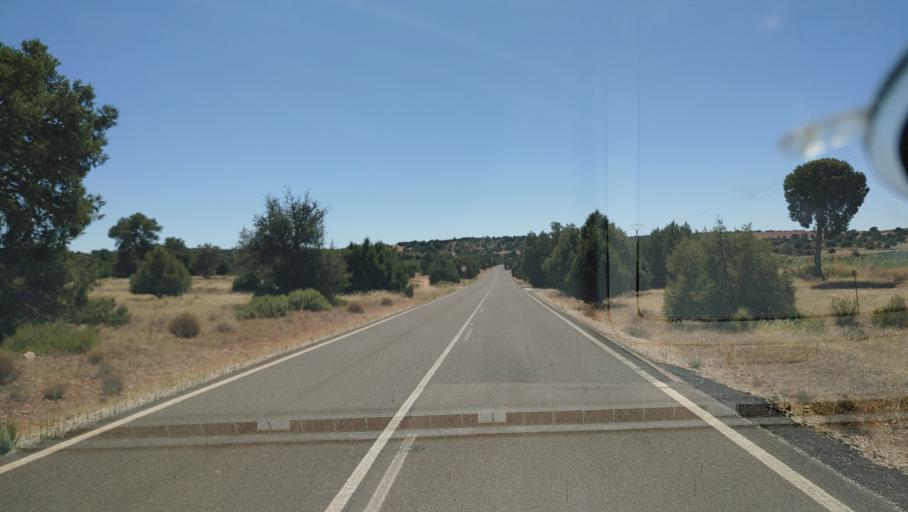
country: ES
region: Castille-La Mancha
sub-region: Provincia de Albacete
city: Ossa de Montiel
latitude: 38.8575
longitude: -2.8017
